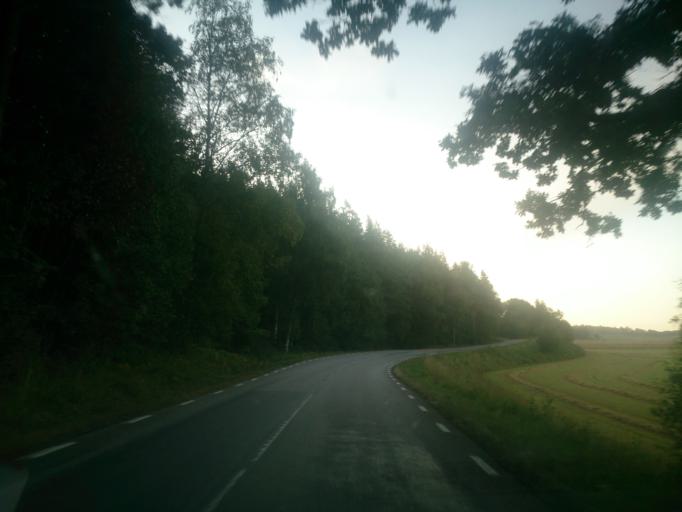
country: SE
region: Soedermanland
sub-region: Nykopings Kommun
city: Nykoping
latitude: 58.8685
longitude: 17.1698
